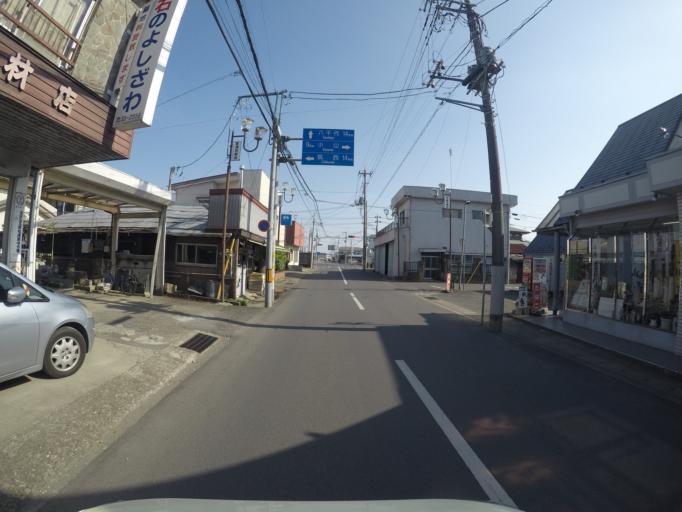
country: JP
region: Ibaraki
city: Yuki
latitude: 36.2971
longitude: 139.8765
